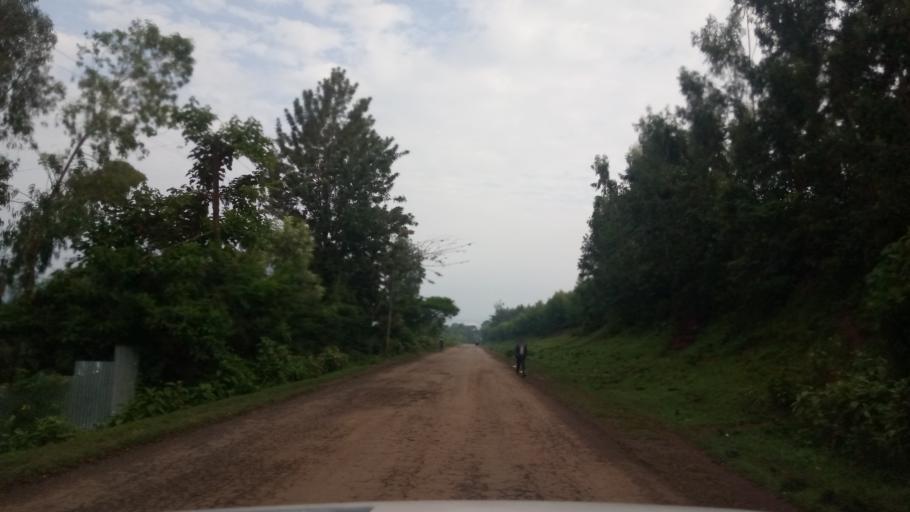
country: ET
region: Oromiya
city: Agaro
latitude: 7.7928
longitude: 36.7249
